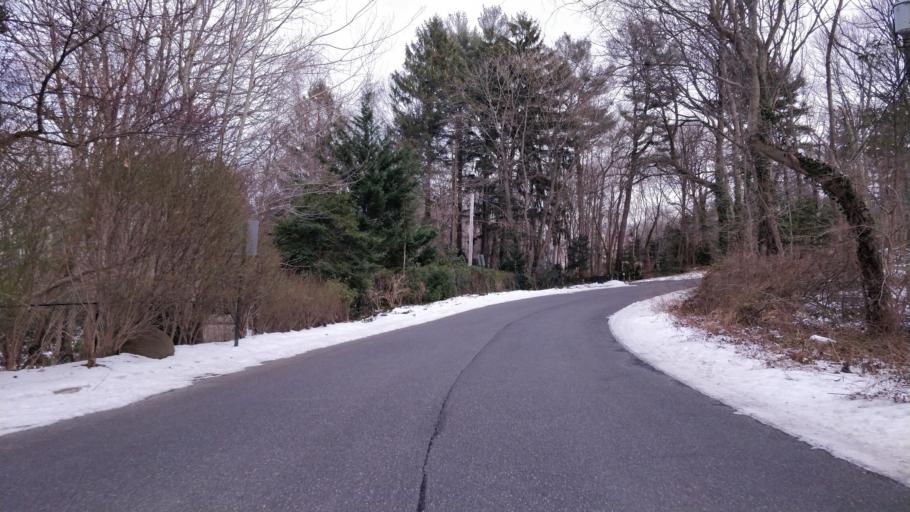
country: US
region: New York
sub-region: Suffolk County
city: Greenlawn
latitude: 40.8782
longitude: -73.3672
